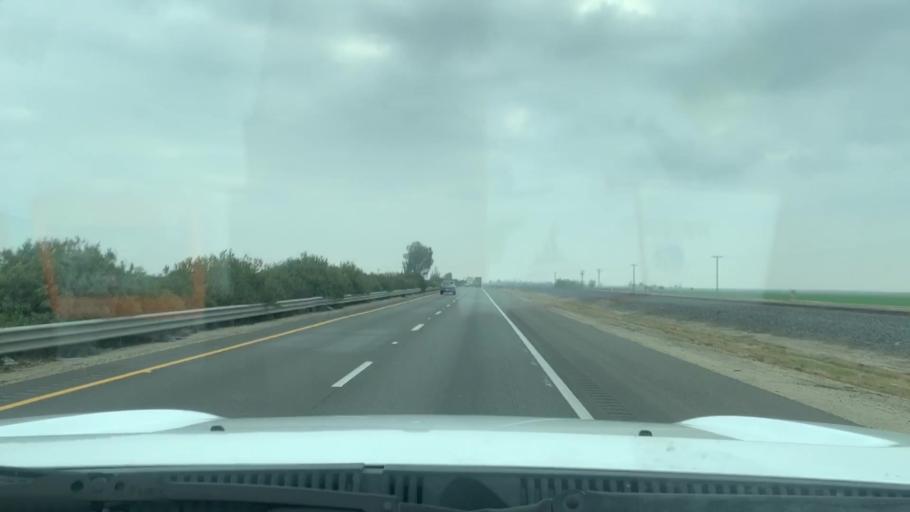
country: US
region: California
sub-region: Tulare County
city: Tipton
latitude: 36.0914
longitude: -119.3217
